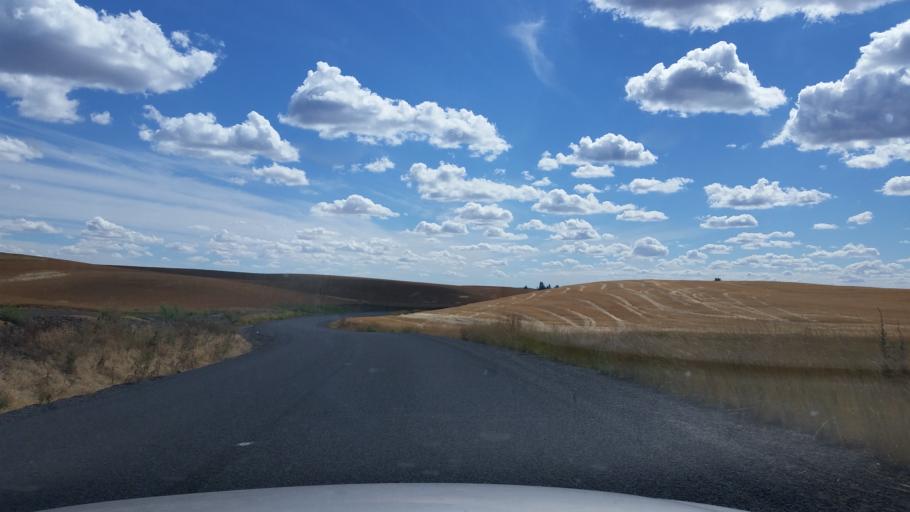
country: US
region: Washington
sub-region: Spokane County
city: Cheney
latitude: 47.4965
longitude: -117.6199
